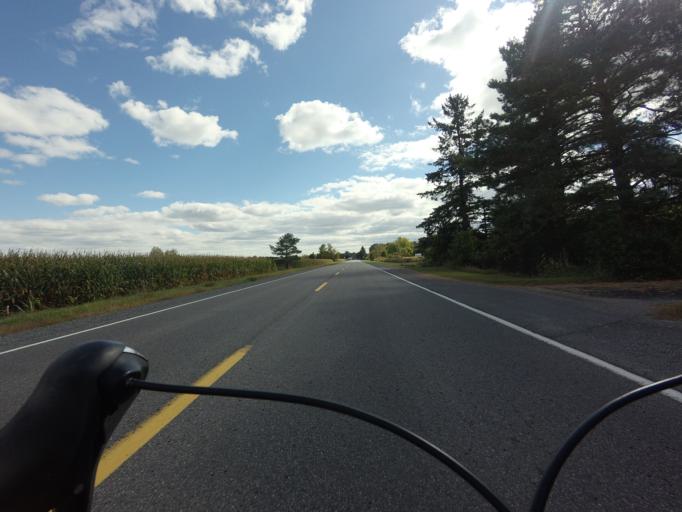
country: CA
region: Ontario
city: Bells Corners
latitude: 45.1633
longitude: -75.6550
